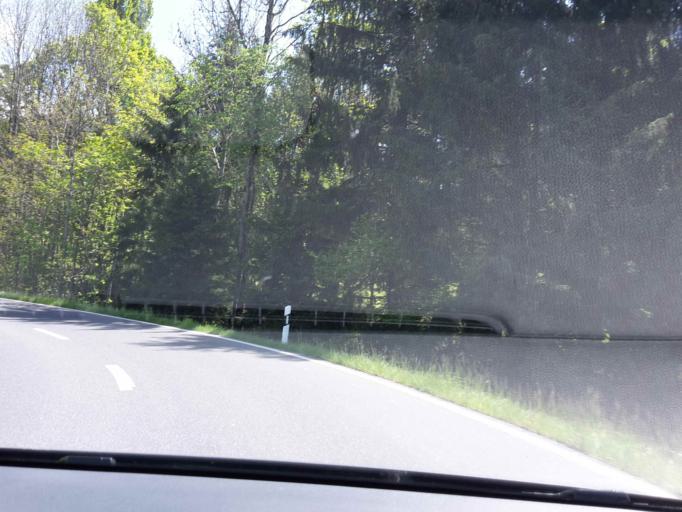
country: CH
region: Bern
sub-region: Thun District
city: Hilterfingen
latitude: 46.7537
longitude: 7.6581
